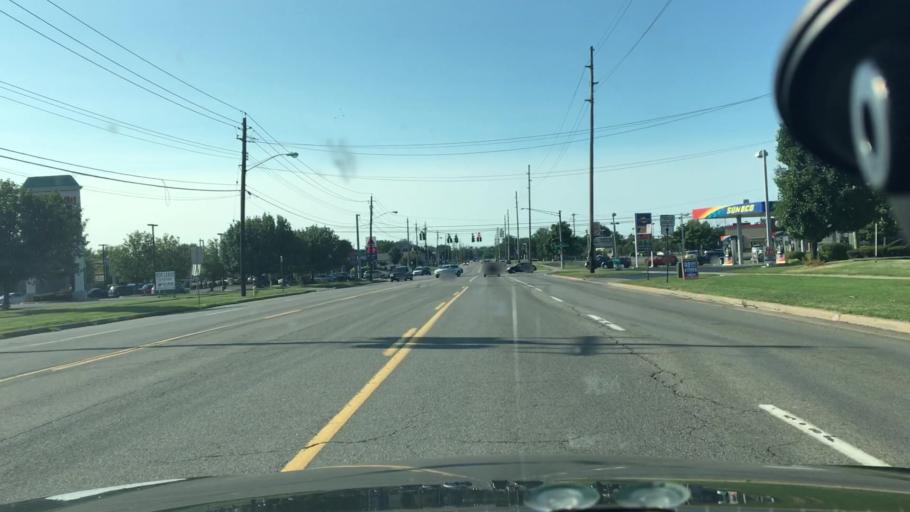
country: US
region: New York
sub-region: Erie County
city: Cheektowaga
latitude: 42.9177
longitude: -78.7367
